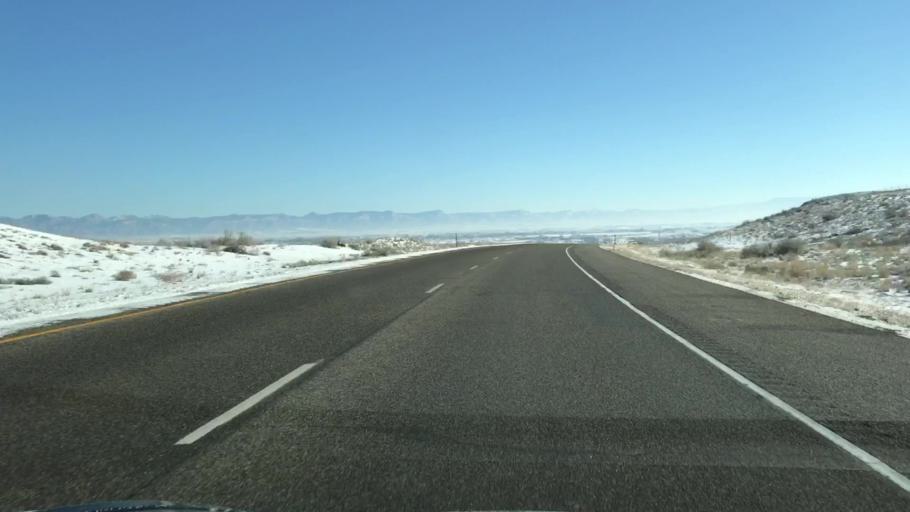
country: US
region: Colorado
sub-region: Mesa County
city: Loma
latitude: 39.2299
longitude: -108.9101
